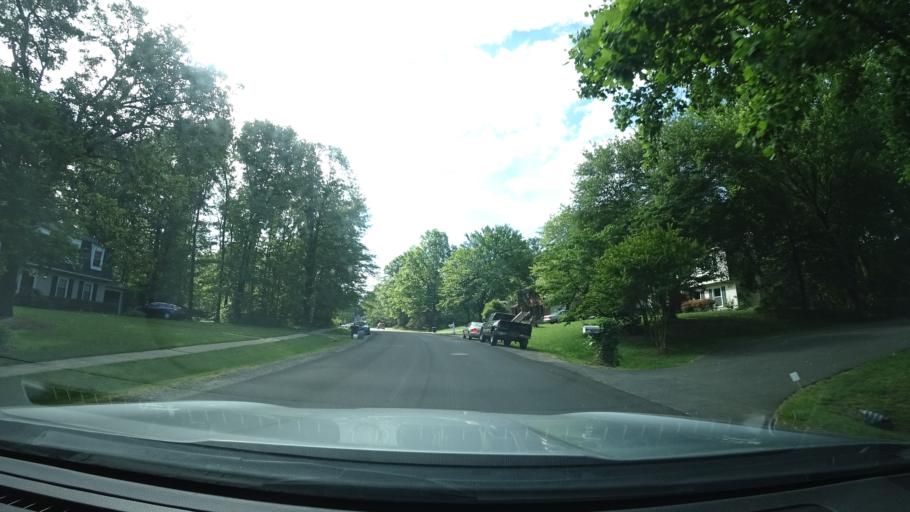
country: US
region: Virginia
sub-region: Fairfax County
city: Oak Hill
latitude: 38.9386
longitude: -77.3789
